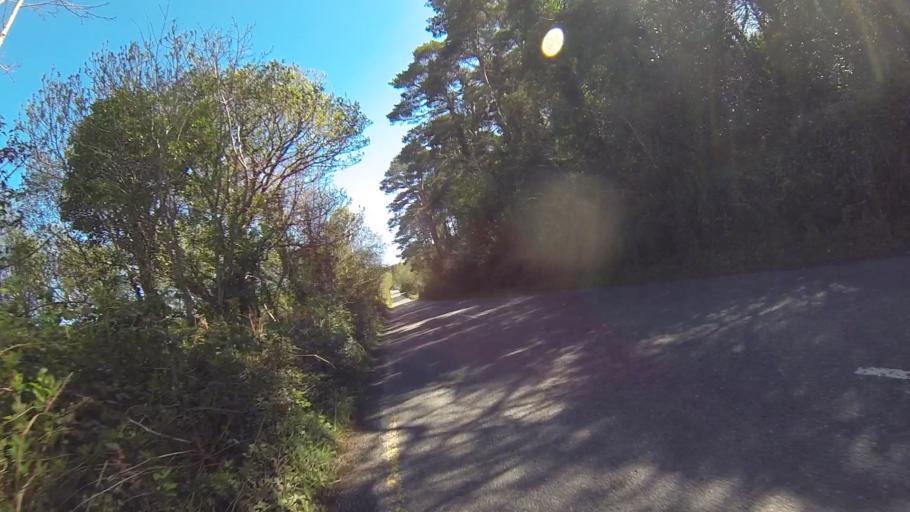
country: IE
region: Munster
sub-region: Ciarrai
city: Kenmare
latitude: 51.8510
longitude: -9.6318
